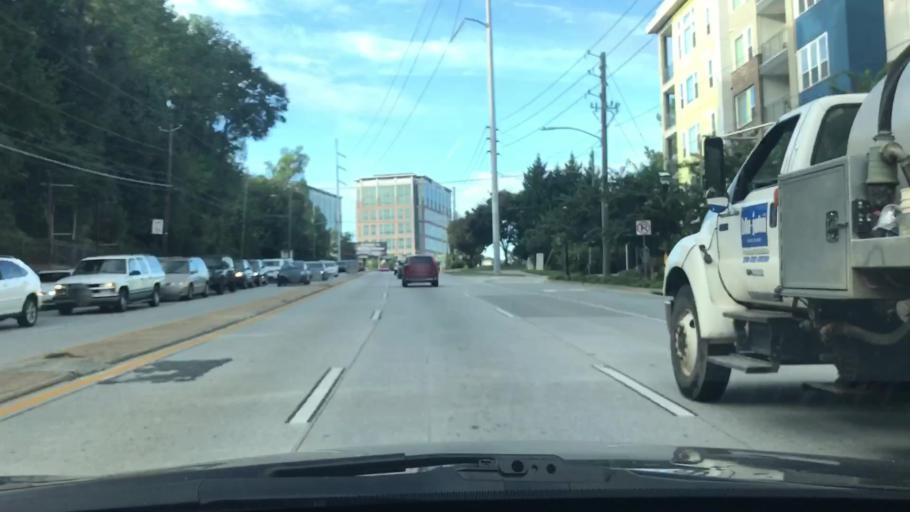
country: US
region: Georgia
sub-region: DeKalb County
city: Druid Hills
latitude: 33.8185
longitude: -84.3671
